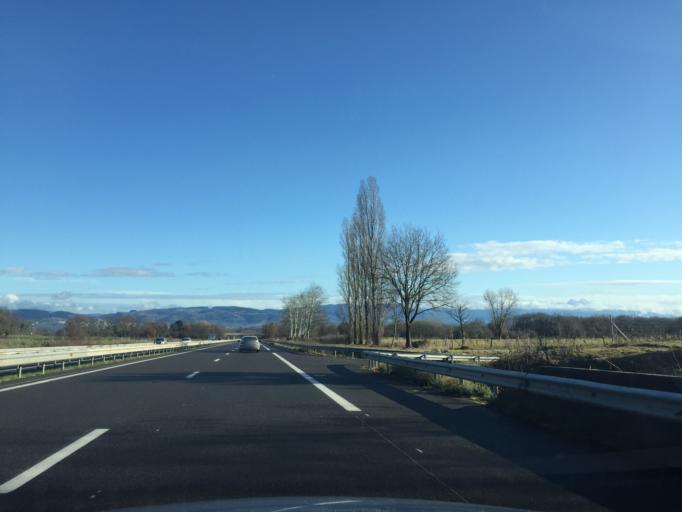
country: FR
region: Auvergne
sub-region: Departement du Puy-de-Dome
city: Orleat
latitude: 45.8506
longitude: 3.4173
